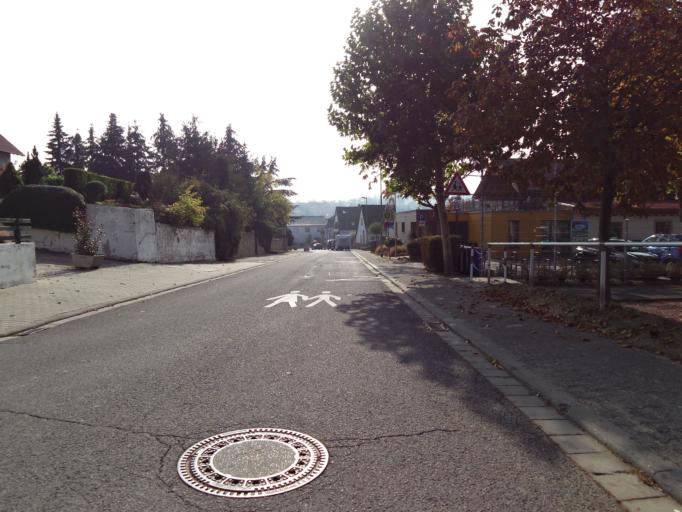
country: DE
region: Rheinland-Pfalz
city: Grunstadt
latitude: 49.5815
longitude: 8.1595
